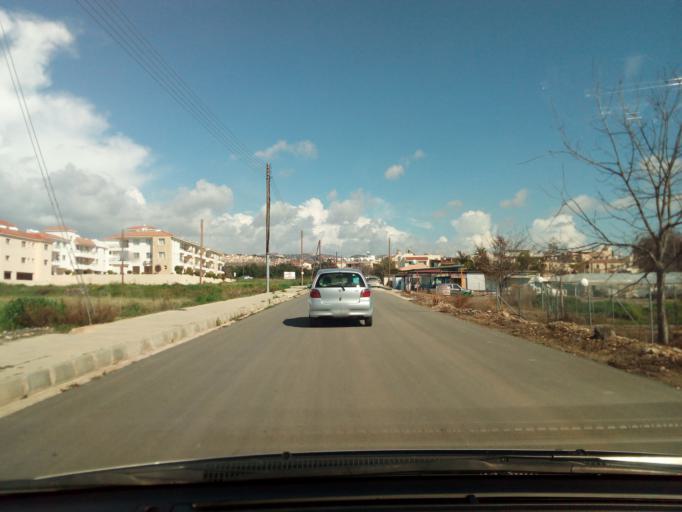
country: CY
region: Pafos
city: Empa
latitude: 34.8097
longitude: 32.4190
